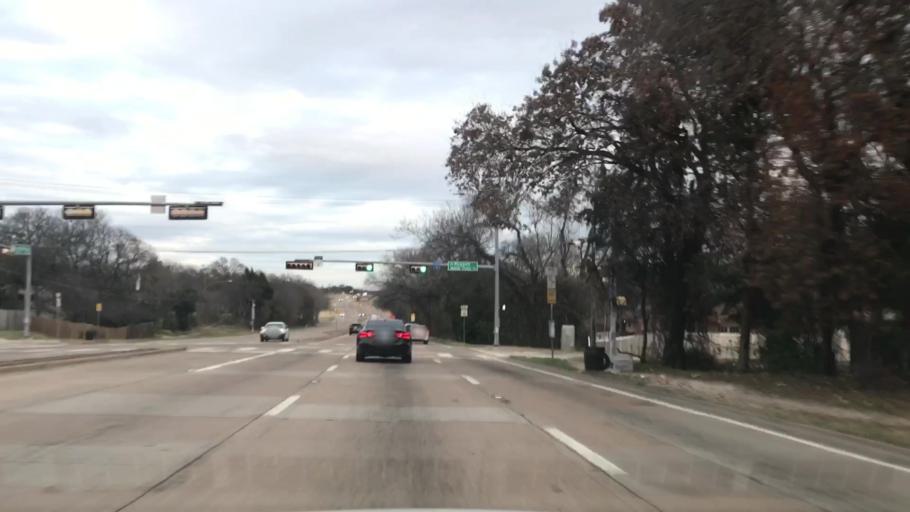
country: US
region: Texas
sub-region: Dallas County
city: Cockrell Hill
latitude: 32.6912
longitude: -96.8526
